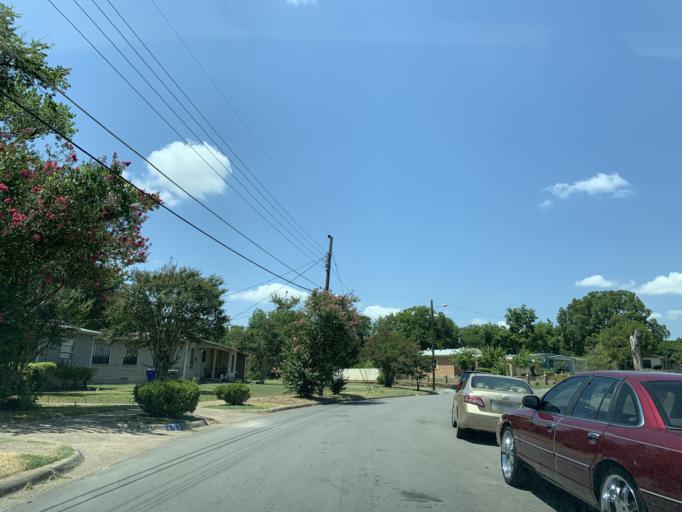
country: US
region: Texas
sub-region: Dallas County
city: Hutchins
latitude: 32.6911
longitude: -96.7729
